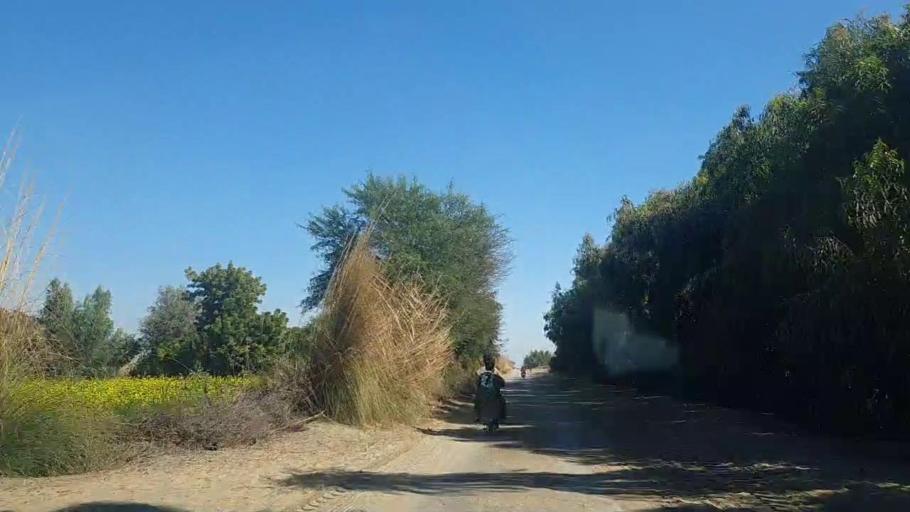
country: PK
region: Sindh
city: Khadro
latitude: 26.2094
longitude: 68.8257
